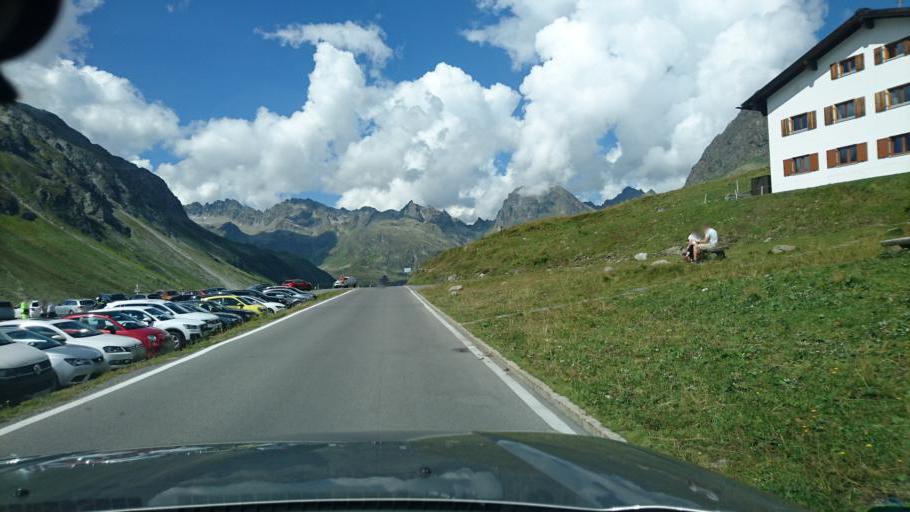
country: AT
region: Vorarlberg
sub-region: Politischer Bezirk Bludenz
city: Gaschurn
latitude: 46.9176
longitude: 10.0927
